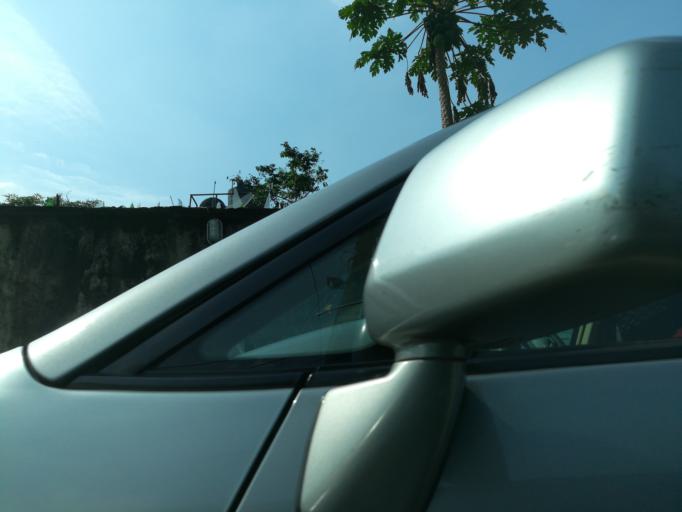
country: NG
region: Rivers
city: Port Harcourt
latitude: 4.8318
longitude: 6.9894
